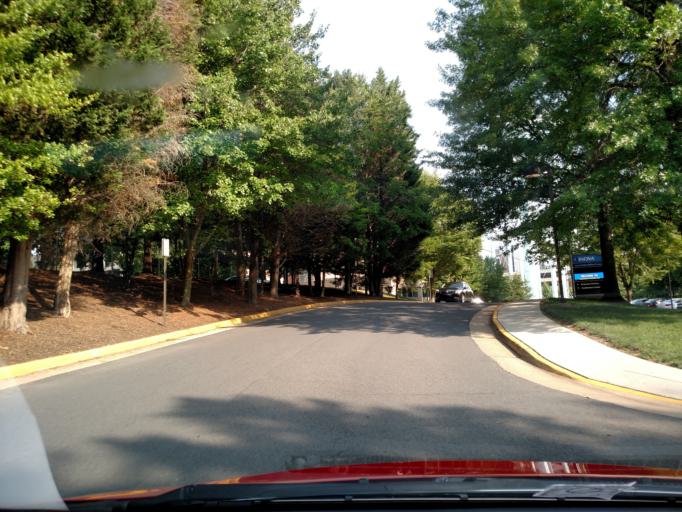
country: US
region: Virginia
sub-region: Fairfax County
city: Merrifield
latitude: 38.8598
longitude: -77.2314
